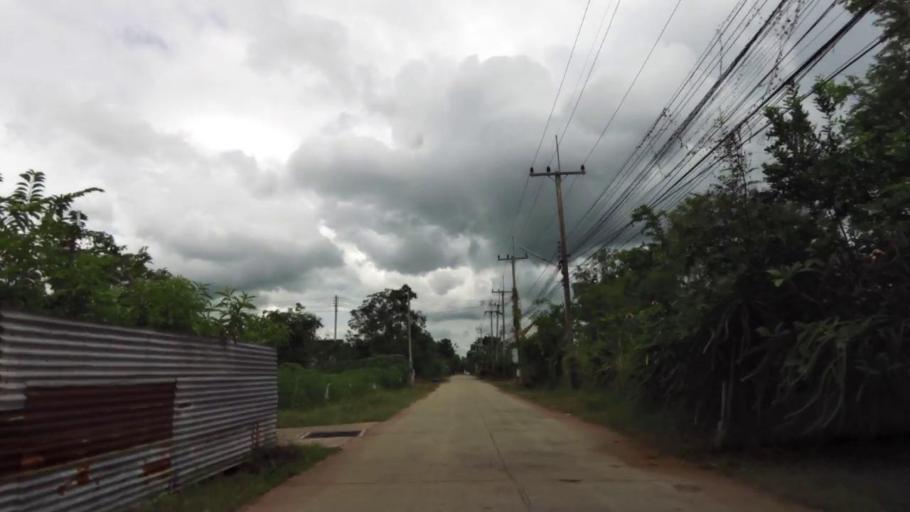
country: TH
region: Nakhon Sawan
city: Phai Sali
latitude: 15.6013
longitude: 100.6625
